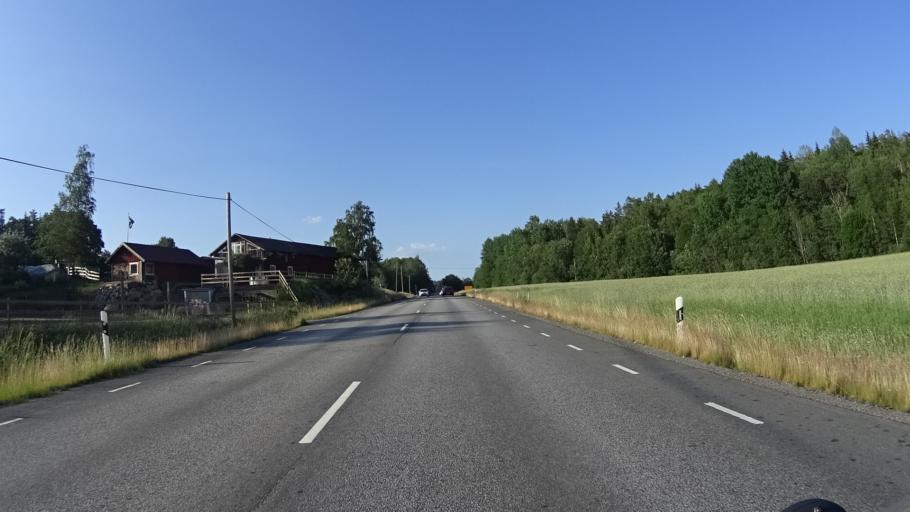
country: SE
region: Stockholm
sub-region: Sodertalje Kommun
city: Pershagen
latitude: 59.0935
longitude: 17.6183
